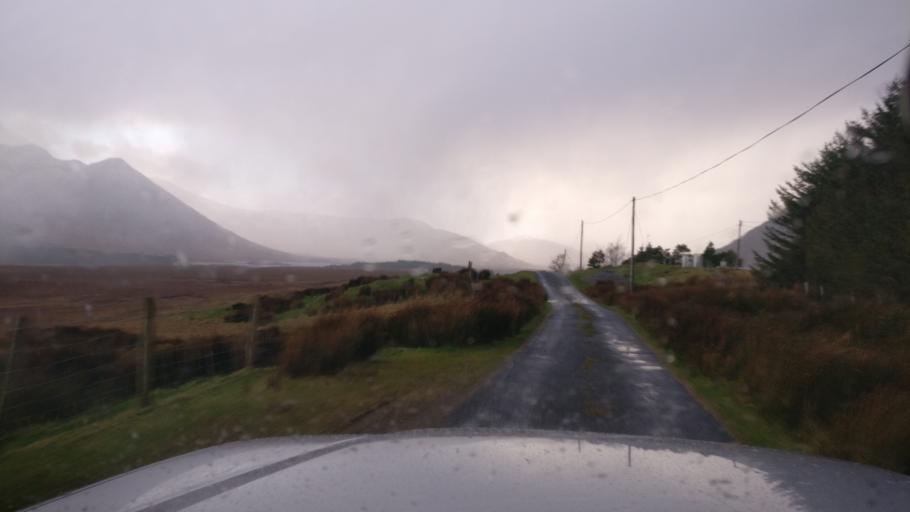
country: IE
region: Connaught
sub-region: County Galway
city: Clifden
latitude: 53.5137
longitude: -9.7130
